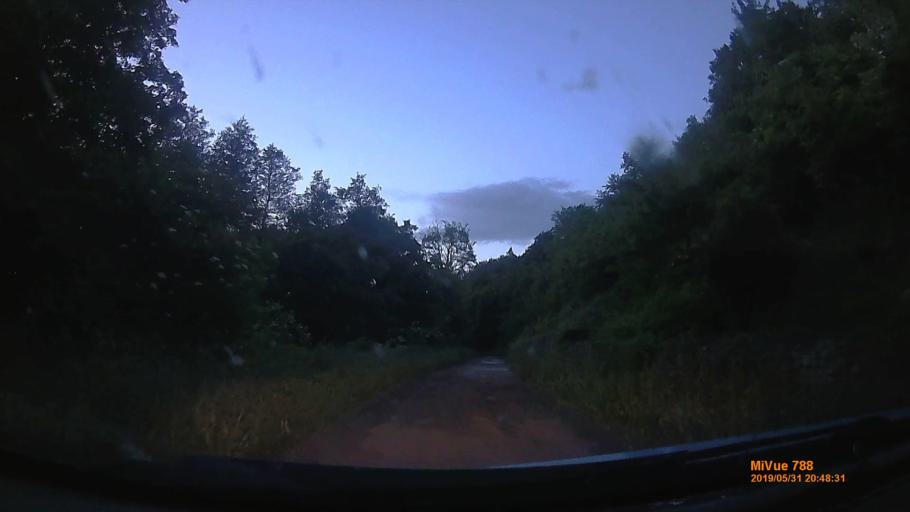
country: HU
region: Nograd
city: Nagyoroszi
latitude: 48.0377
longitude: 19.0466
